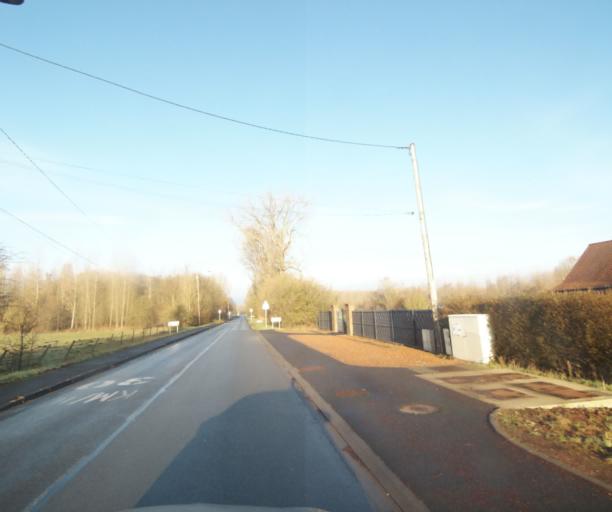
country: FR
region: Nord-Pas-de-Calais
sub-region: Departement du Nord
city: Onnaing
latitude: 50.3959
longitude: 3.5907
